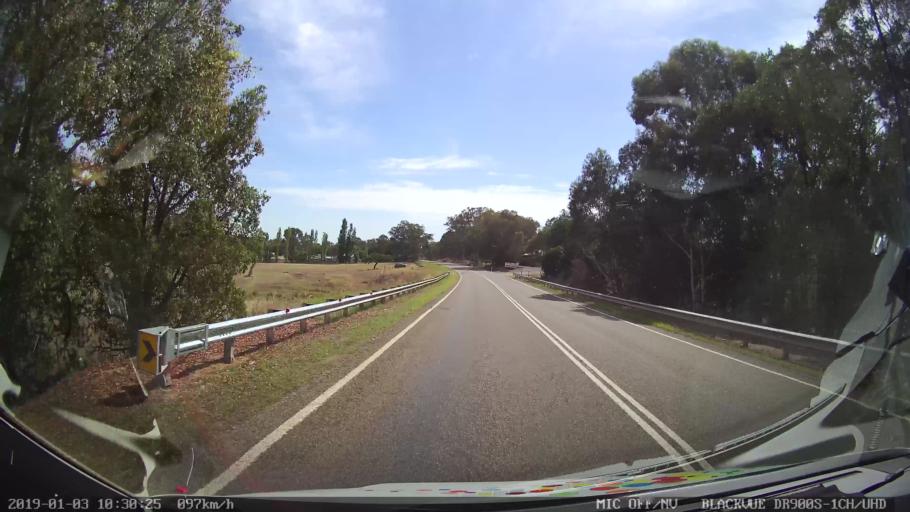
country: AU
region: New South Wales
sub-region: Young
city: Young
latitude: -34.3623
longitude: 148.2680
